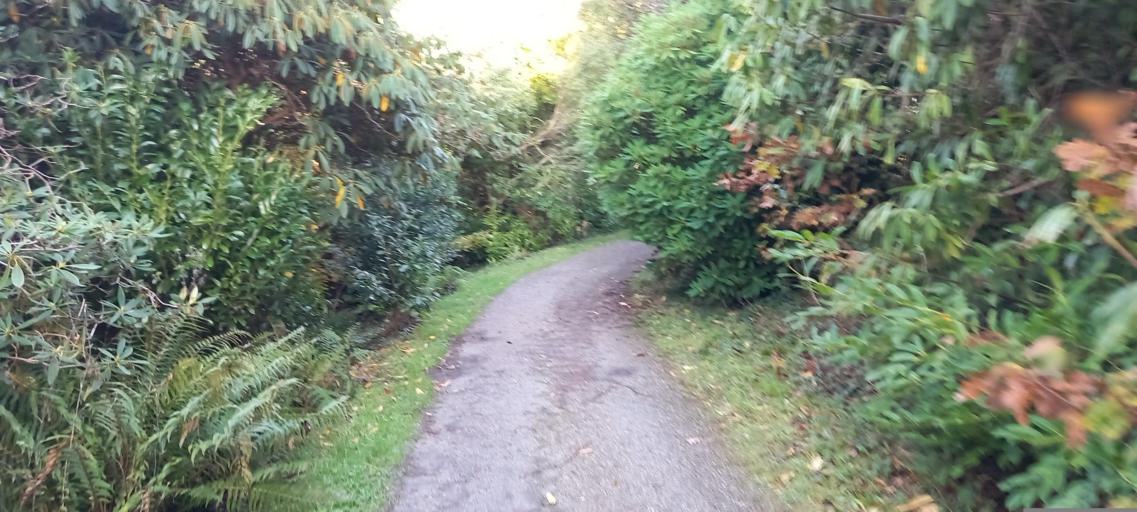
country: GB
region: Wales
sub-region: Gwynedd
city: Bangor
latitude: 53.2273
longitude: -4.0983
